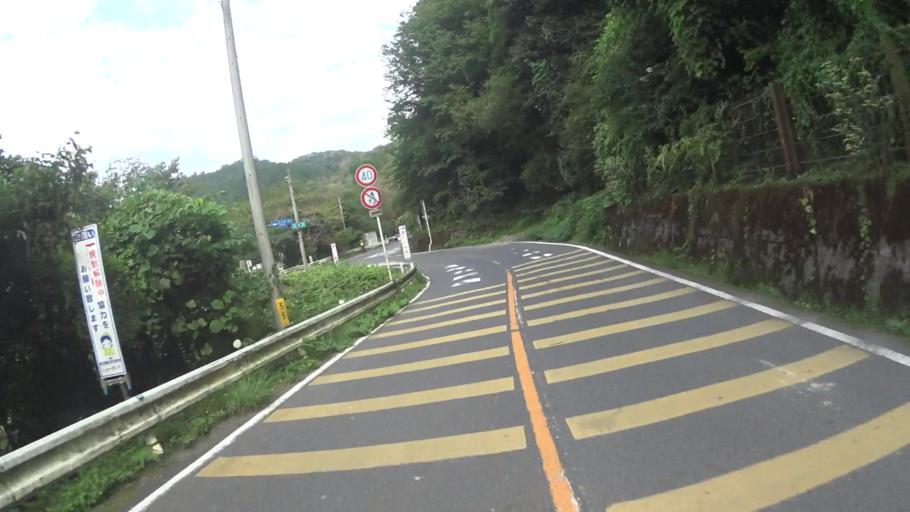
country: JP
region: Kyoto
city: Uji
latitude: 34.9067
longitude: 135.8675
